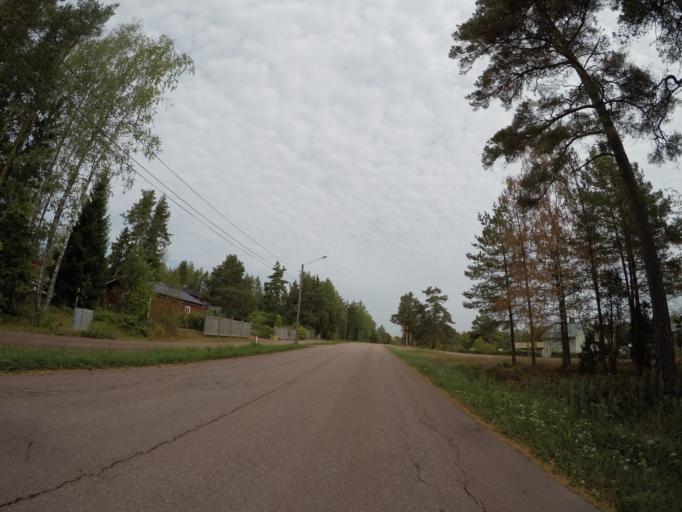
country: AX
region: Alands landsbygd
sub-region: Finstroem
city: Finstroem
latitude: 60.2212
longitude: 19.9806
